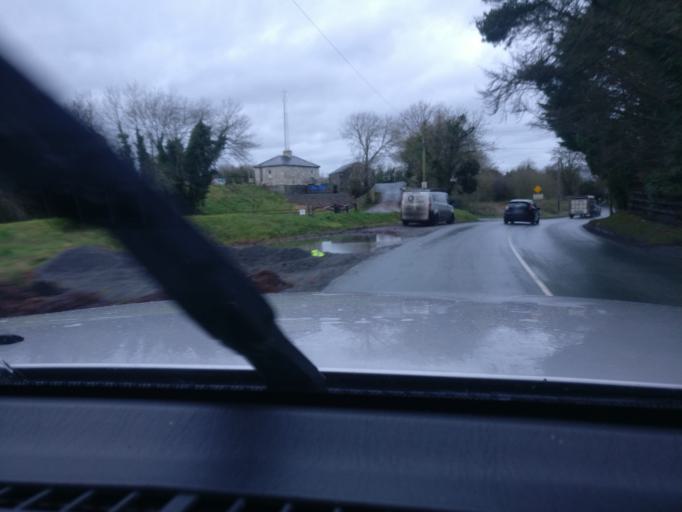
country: IE
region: Leinster
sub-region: An Mhi
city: Longwood
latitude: 53.4509
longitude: -6.9541
